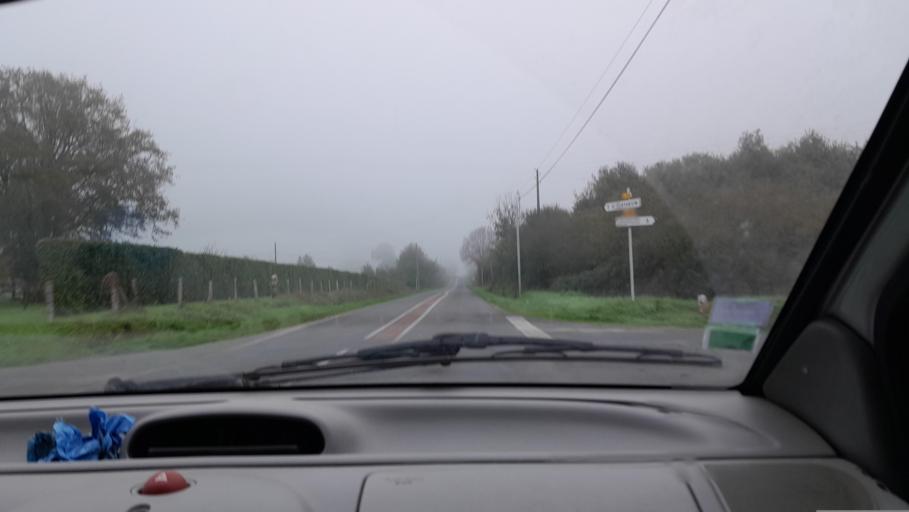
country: FR
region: Pays de la Loire
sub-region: Departement de la Mayenne
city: Ahuille
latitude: 48.0358
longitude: -0.8979
